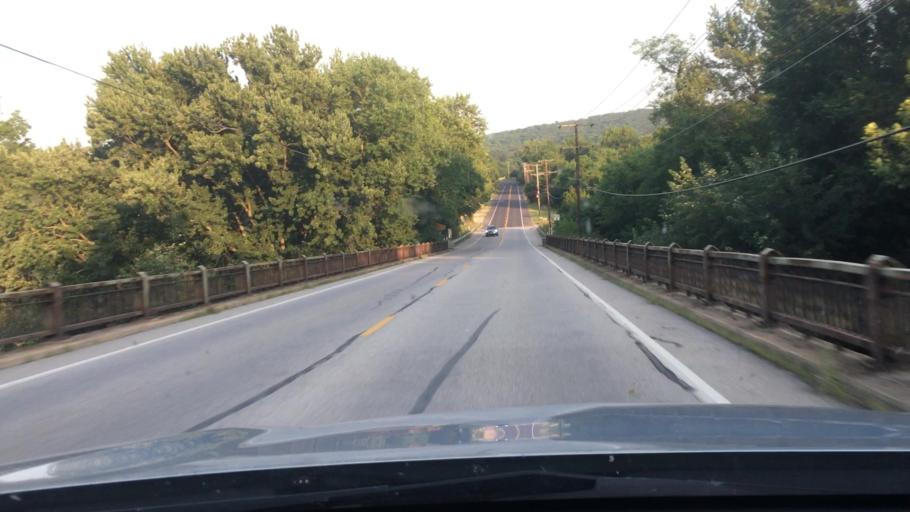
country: US
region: Pennsylvania
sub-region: York County
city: Dover
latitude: 40.0451
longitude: -76.8989
